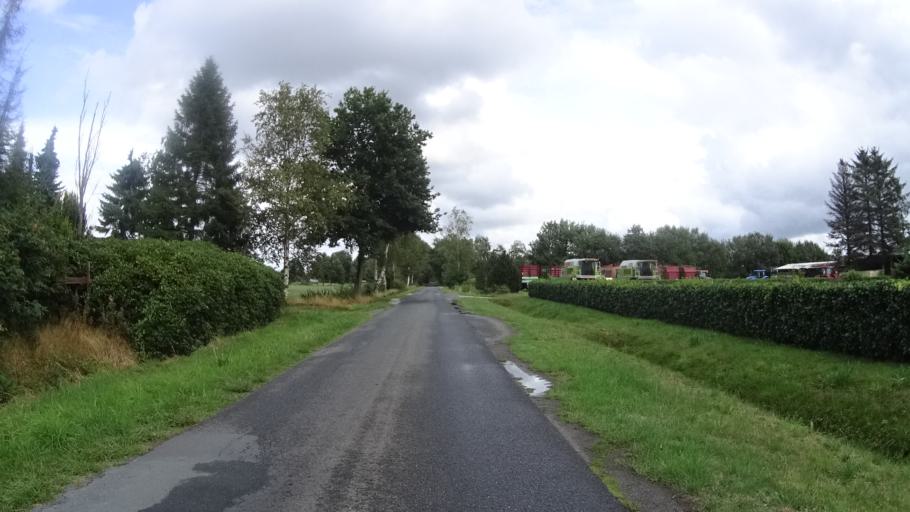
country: DE
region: Lower Saxony
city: Friedeburg
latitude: 53.3785
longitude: 7.8435
